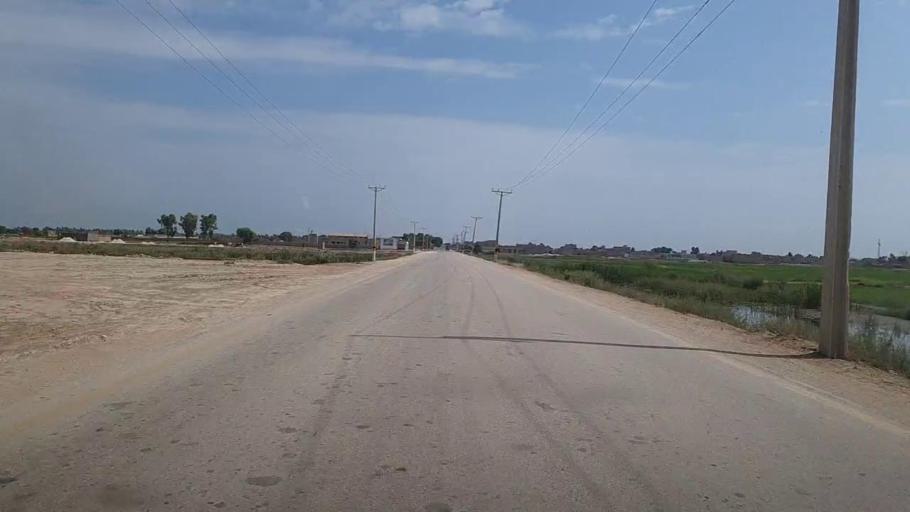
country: PK
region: Sindh
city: Thul
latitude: 28.2507
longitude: 68.7822
